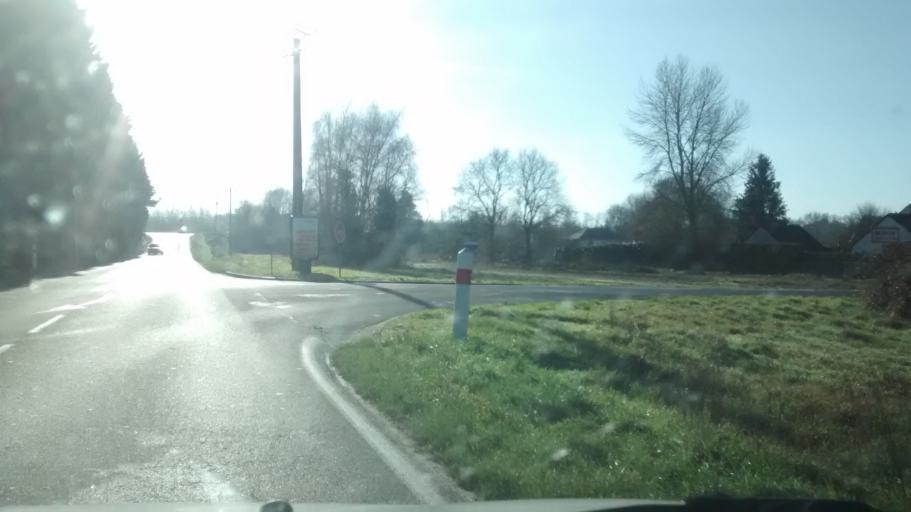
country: FR
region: Centre
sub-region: Departement d'Indre-et-Loire
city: Amboise
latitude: 47.4152
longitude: 0.9627
